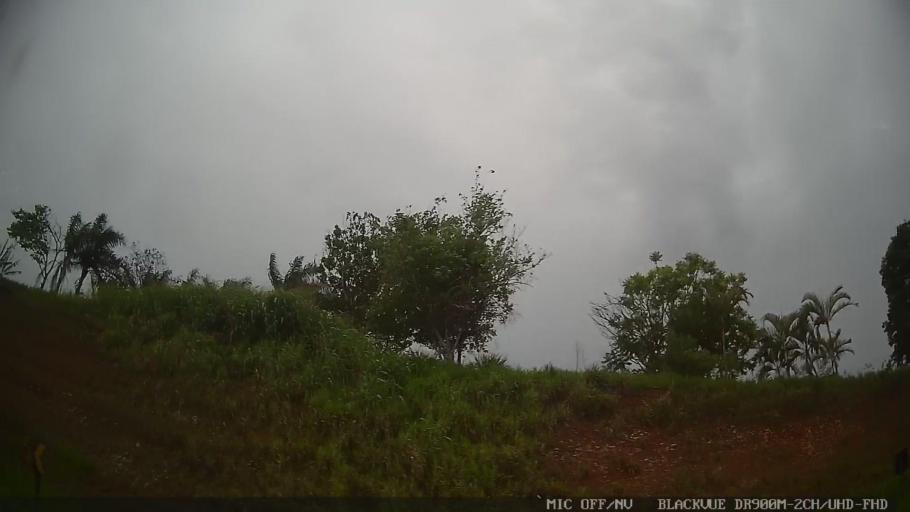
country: BR
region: Sao Paulo
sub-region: Pedreira
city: Pedreira
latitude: -22.7312
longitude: -46.8612
